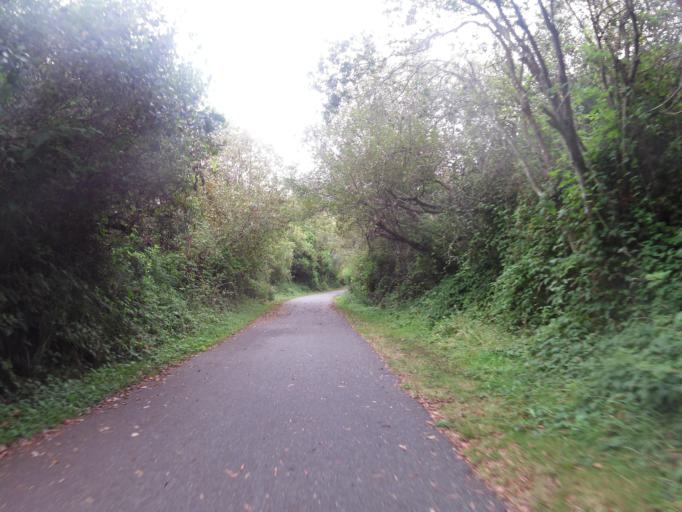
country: US
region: California
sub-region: Humboldt County
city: Bayview
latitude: 40.7642
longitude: -124.1964
